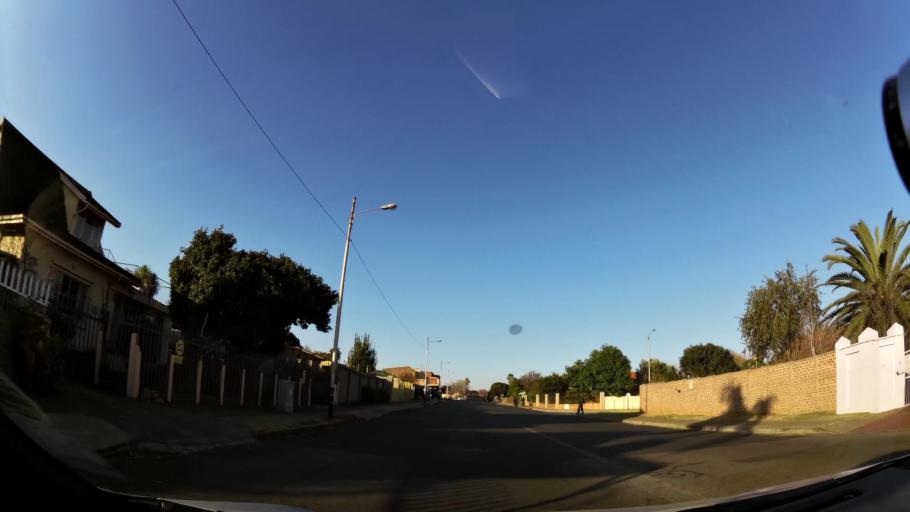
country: ZA
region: Gauteng
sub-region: Ekurhuleni Metropolitan Municipality
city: Germiston
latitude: -26.2660
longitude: 28.1279
